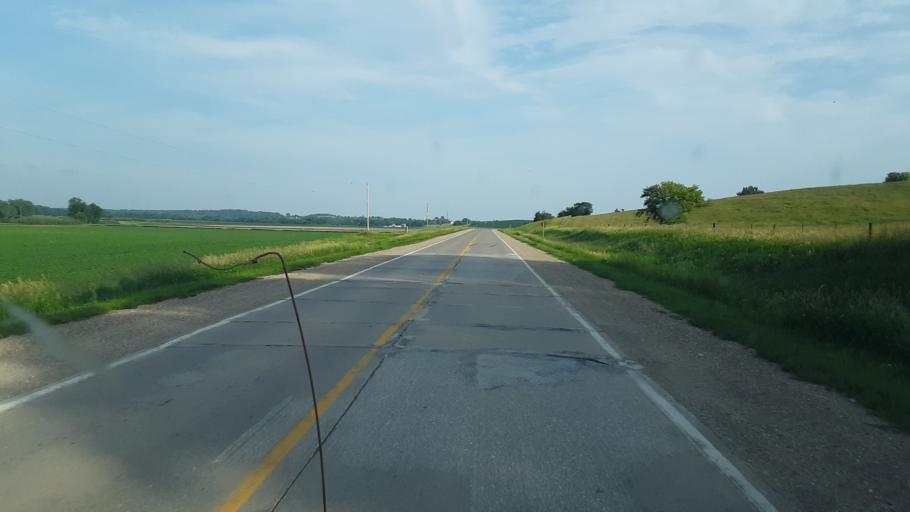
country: US
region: Iowa
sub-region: Tama County
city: Toledo
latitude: 42.0003
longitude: -92.7292
